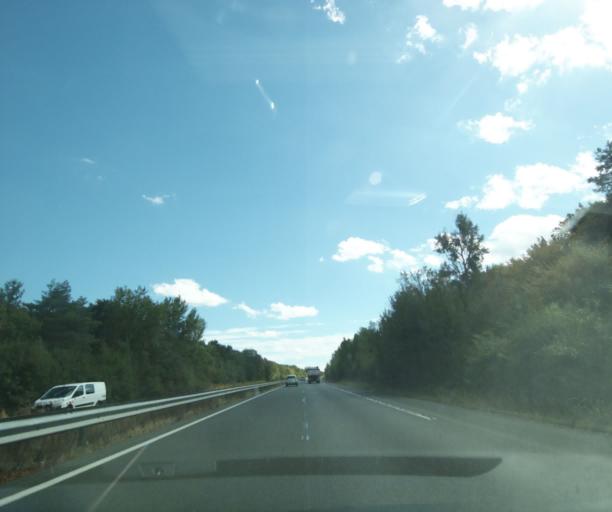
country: FR
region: Aquitaine
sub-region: Departement du Lot-et-Garonne
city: Fourques-sur-Garonne
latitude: 44.4159
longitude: 0.1766
